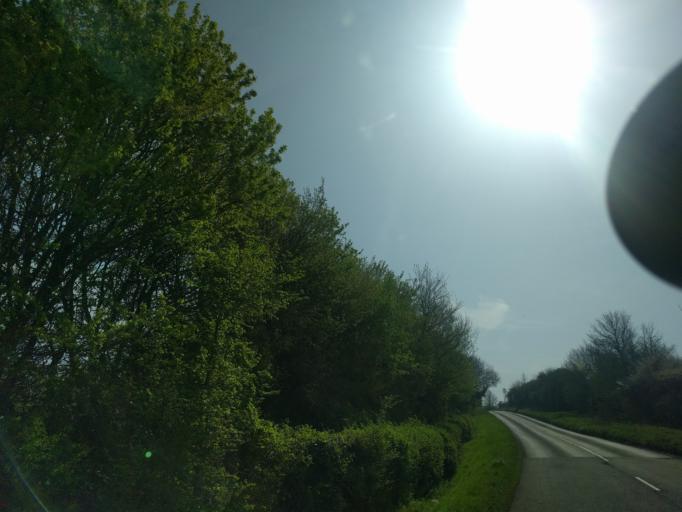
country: GB
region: England
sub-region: Wiltshire
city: Worton
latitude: 51.3072
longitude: -2.0203
